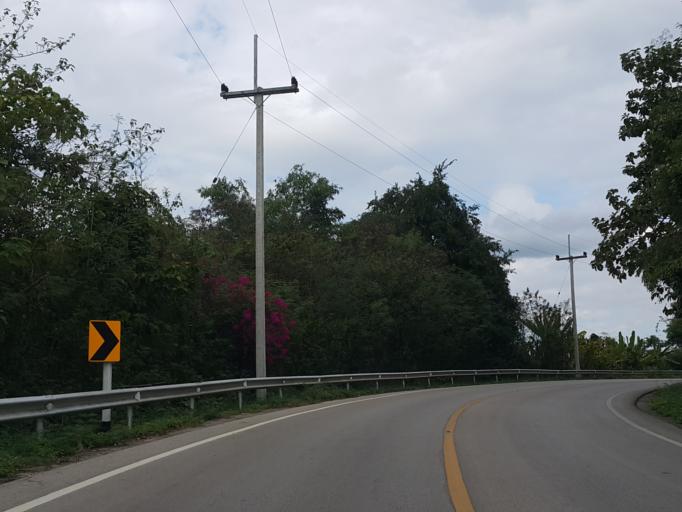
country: TH
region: Lampang
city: Chae Hom
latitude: 18.6049
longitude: 99.4804
